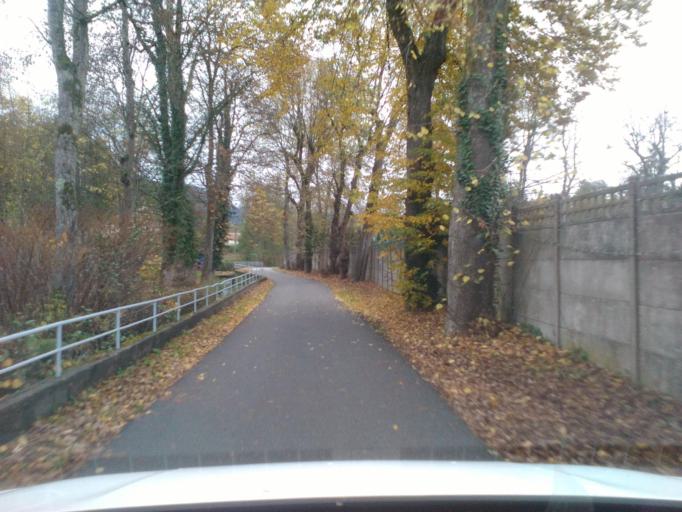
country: FR
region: Lorraine
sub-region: Departement des Vosges
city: Senones
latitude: 48.3977
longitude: 6.9854
